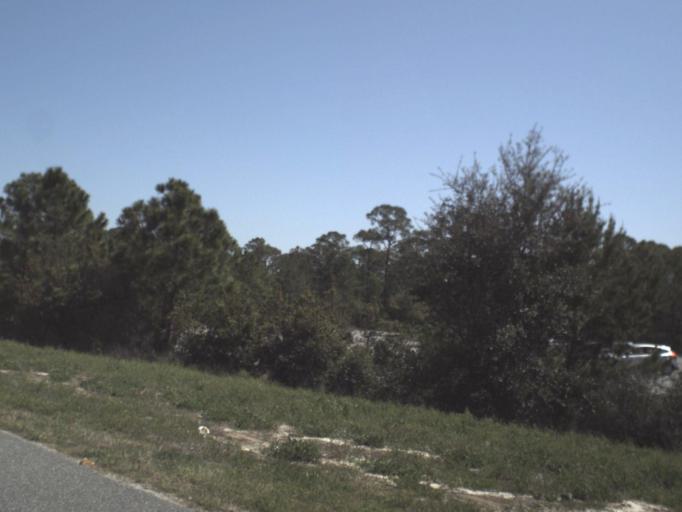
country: US
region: Florida
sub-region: Bay County
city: Mexico Beach
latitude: 29.8892
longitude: -85.3547
